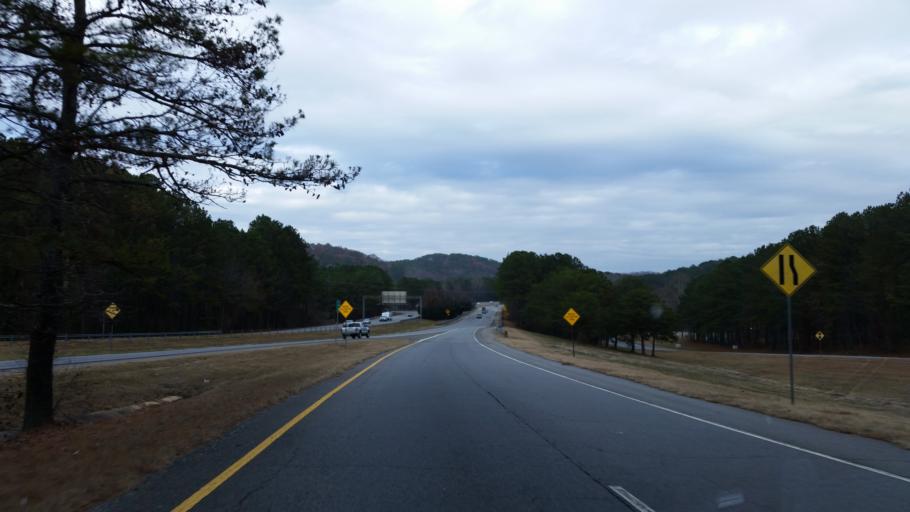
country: US
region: Georgia
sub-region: Cherokee County
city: Canton
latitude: 34.2214
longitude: -84.4866
